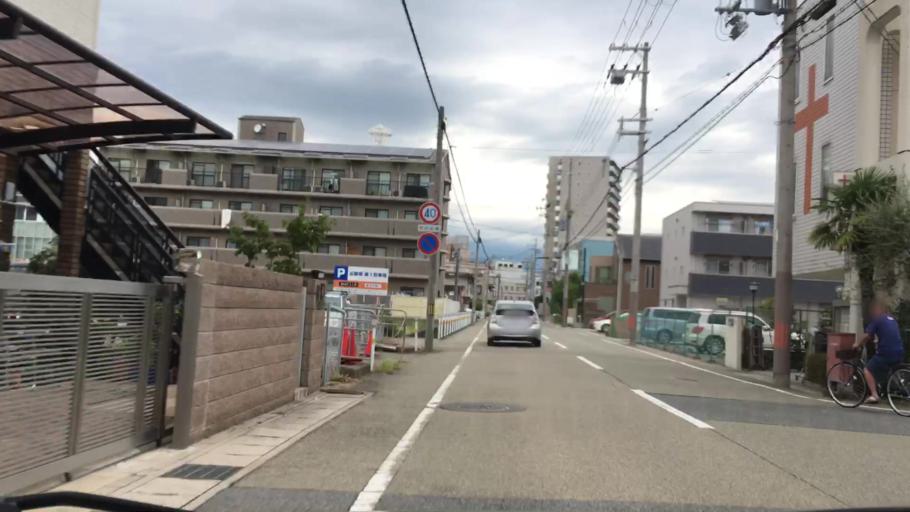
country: JP
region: Hyogo
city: Himeji
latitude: 34.8196
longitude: 134.6933
